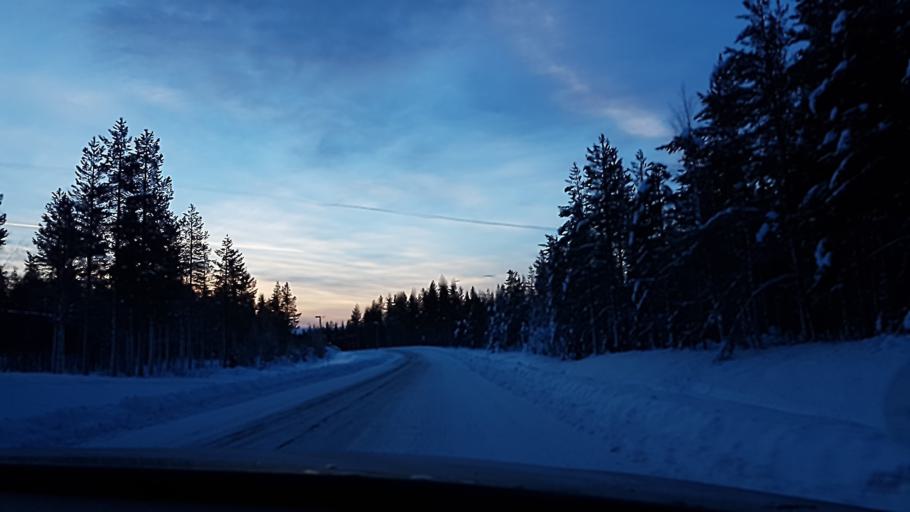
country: SE
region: Norrbotten
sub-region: Jokkmokks Kommun
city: Jokkmokk
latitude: 66.1351
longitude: 20.0006
